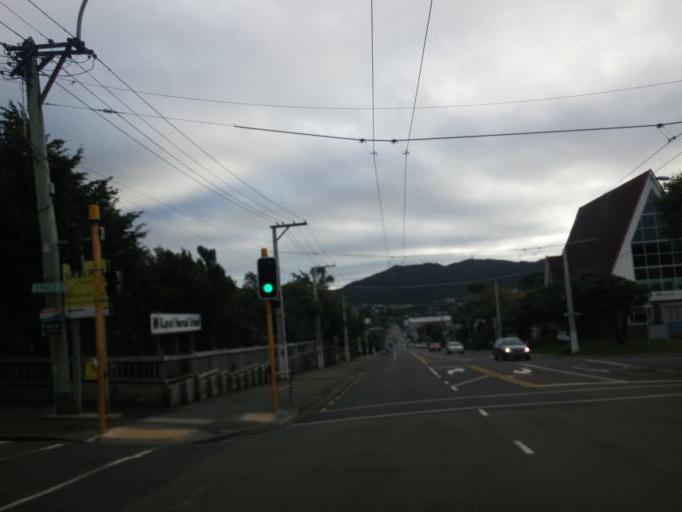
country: NZ
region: Wellington
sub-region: Wellington City
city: Kelburn
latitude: -41.2835
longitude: 174.7419
